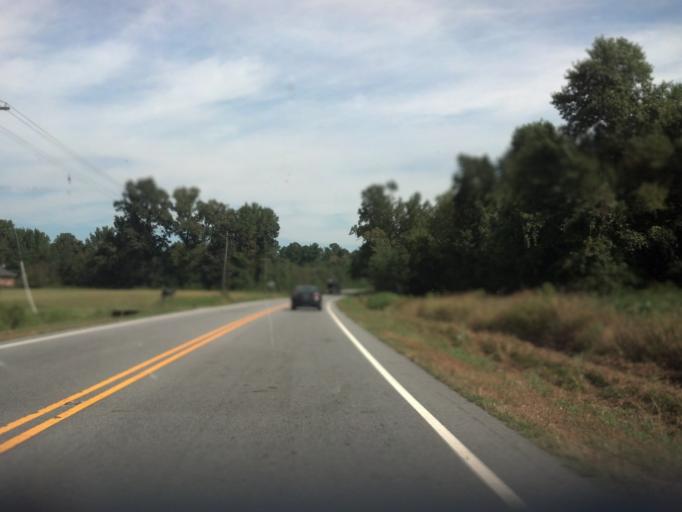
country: US
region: North Carolina
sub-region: Greene County
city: Maury
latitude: 35.5266
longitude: -77.6113
